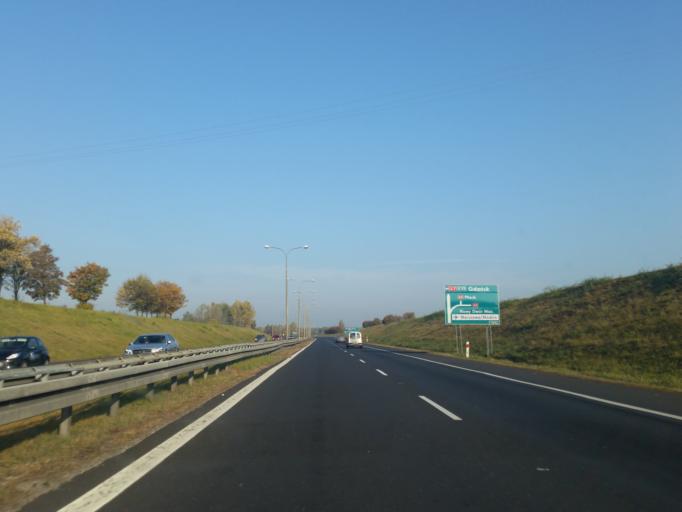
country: PL
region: Masovian Voivodeship
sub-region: Powiat nowodworski
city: Zakroczym
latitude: 52.4347
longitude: 20.6496
